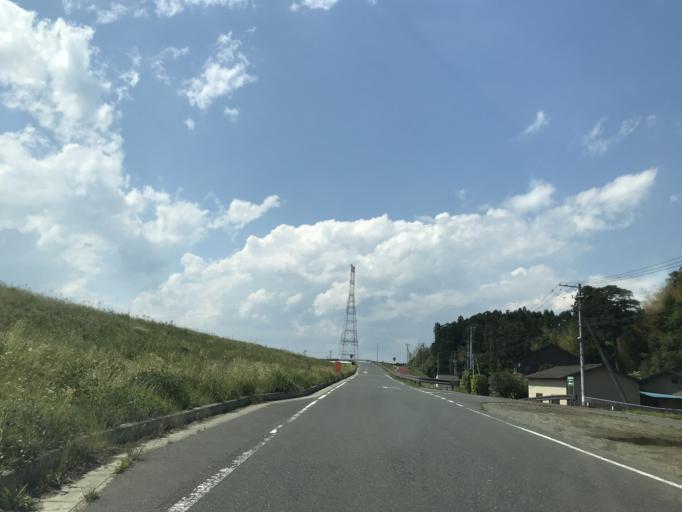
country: JP
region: Miyagi
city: Matsushima
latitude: 38.4269
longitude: 141.1266
